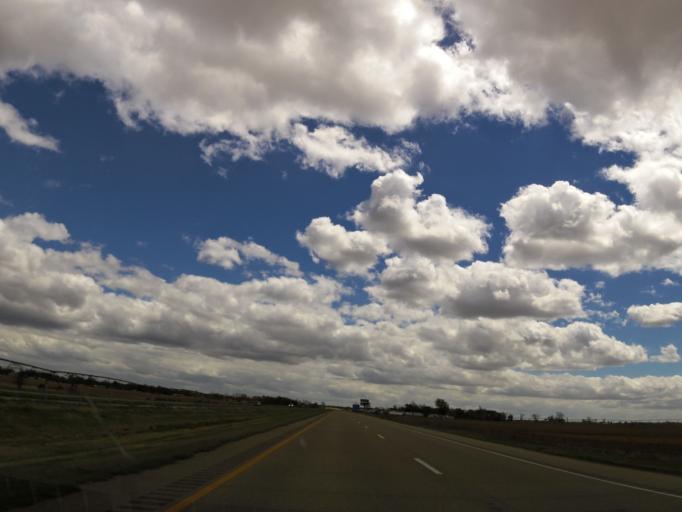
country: US
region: Arkansas
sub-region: Poinsett County
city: Marked Tree
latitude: 35.4964
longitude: -90.3775
